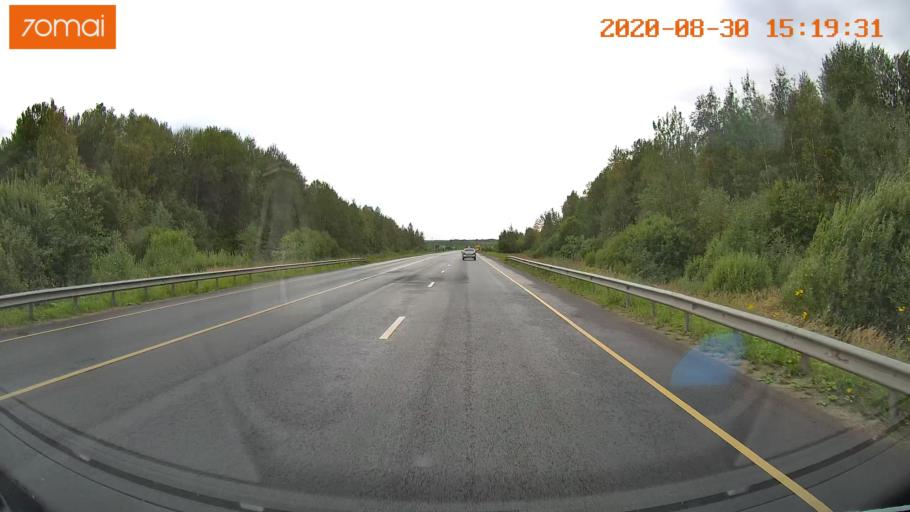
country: RU
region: Ivanovo
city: Rodniki
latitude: 57.1106
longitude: 41.7819
